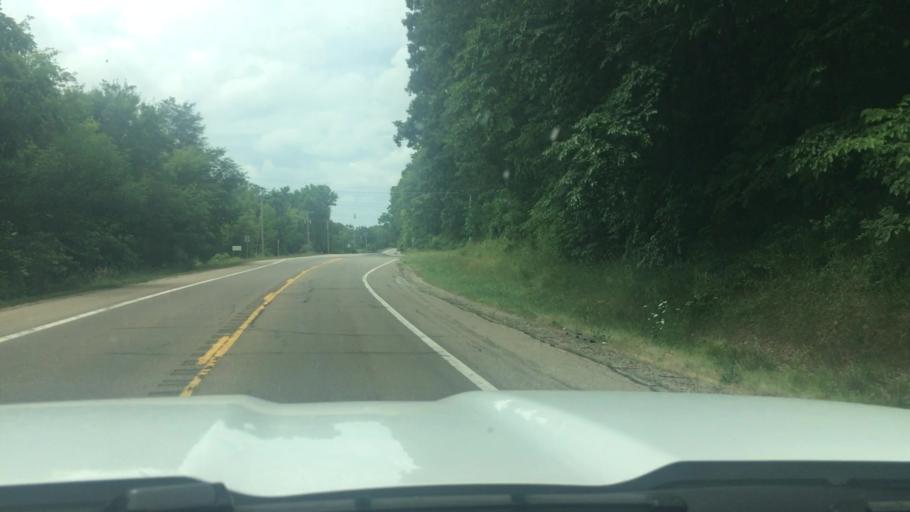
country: US
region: Michigan
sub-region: Kent County
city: Lowell
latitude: 42.9256
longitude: -85.4164
